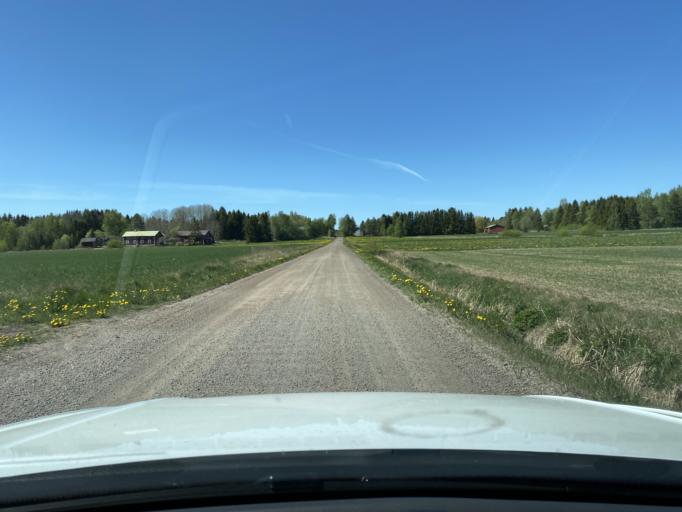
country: FI
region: Satakunta
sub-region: Rauma
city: Lappi
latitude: 61.1382
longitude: 21.9623
